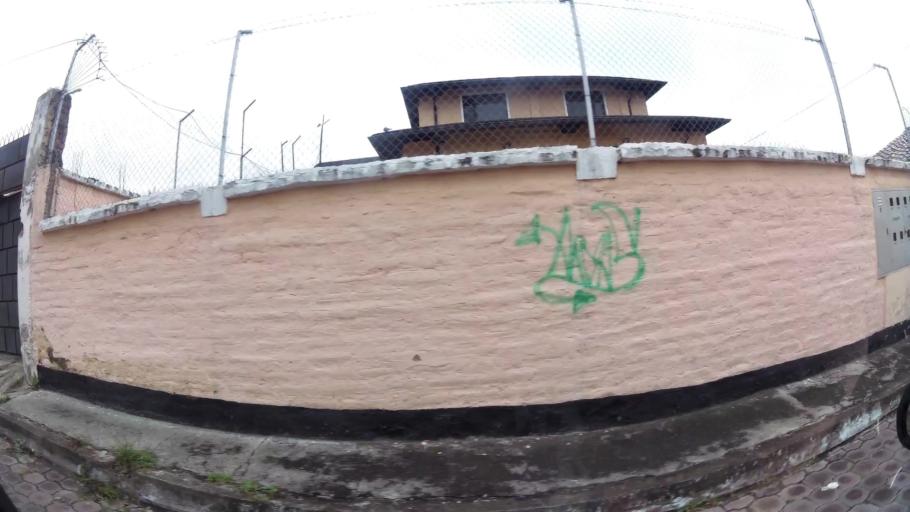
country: EC
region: Pichincha
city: Sangolqui
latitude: -0.2970
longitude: -78.4661
